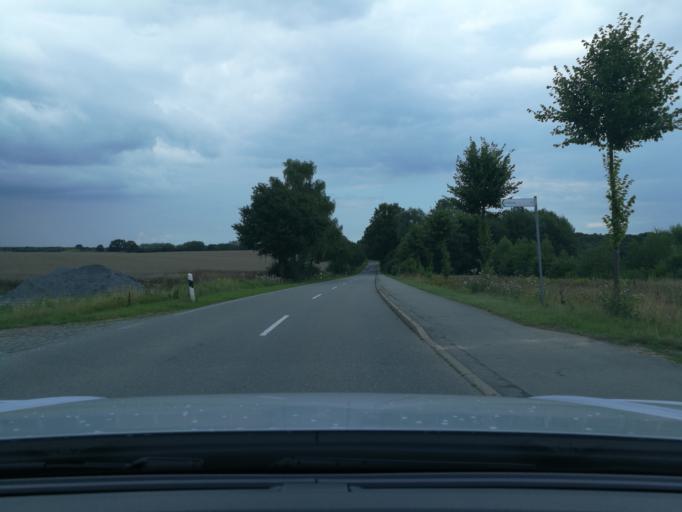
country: DE
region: Schleswig-Holstein
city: Reinbek
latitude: 53.5347
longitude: 10.2626
